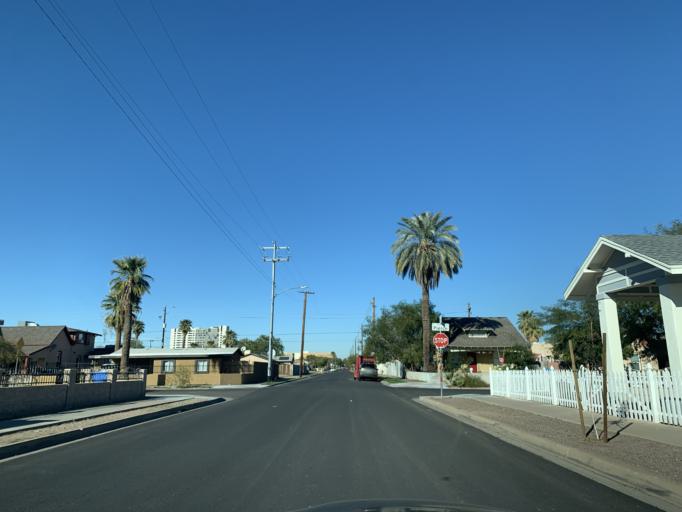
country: US
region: Arizona
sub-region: Maricopa County
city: Phoenix
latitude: 33.4555
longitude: -112.0564
